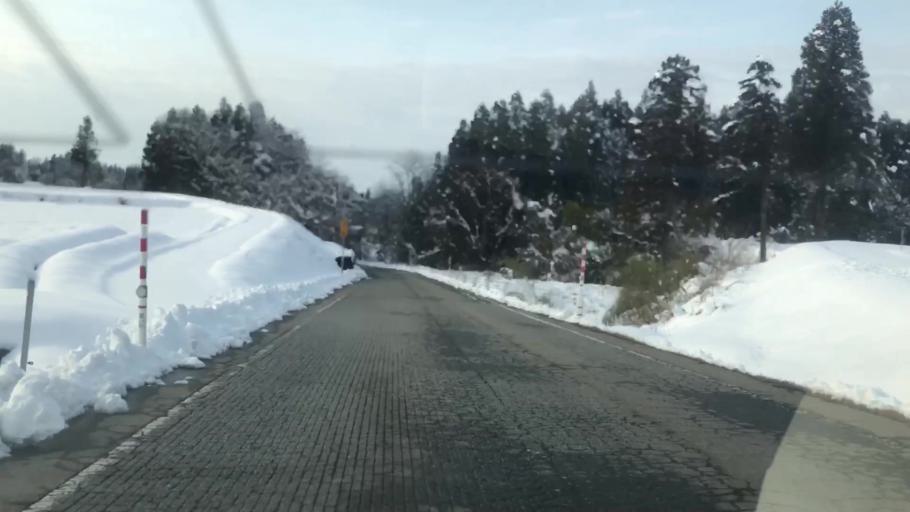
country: JP
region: Toyama
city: Kamiichi
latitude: 36.6036
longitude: 137.3073
